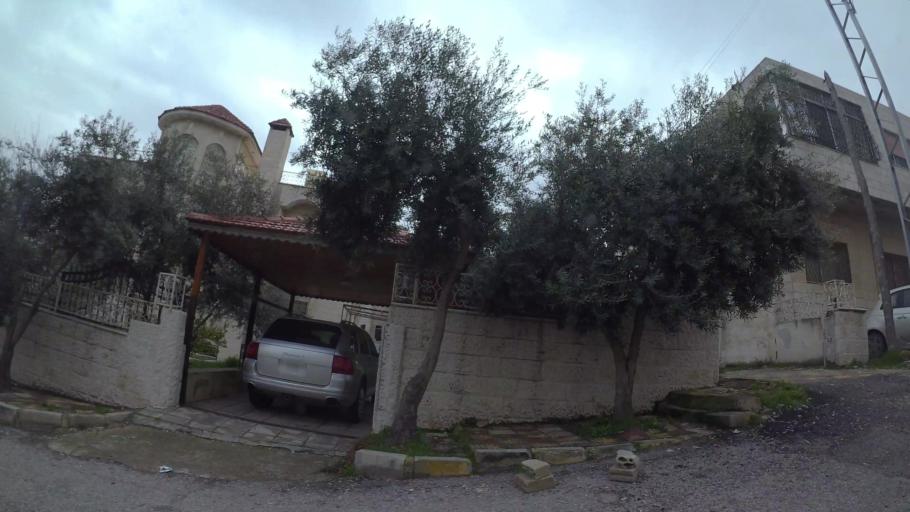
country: JO
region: Amman
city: Umm as Summaq
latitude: 31.9037
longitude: 35.8510
